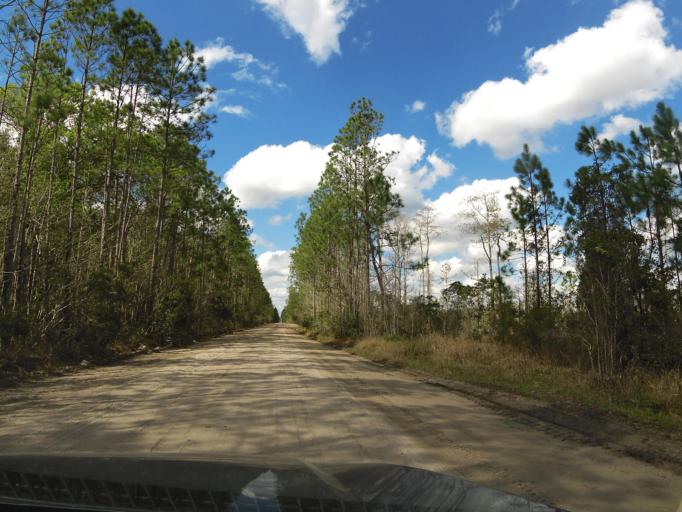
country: US
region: Florida
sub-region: Clay County
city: Green Cove Springs
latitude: 29.8373
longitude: -81.7413
